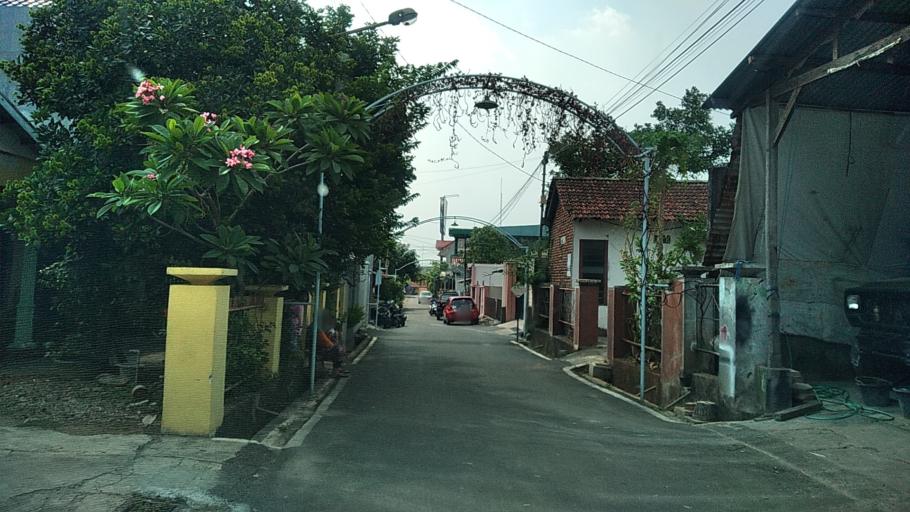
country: ID
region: Central Java
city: Semarang
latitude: -7.0472
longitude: 110.4220
